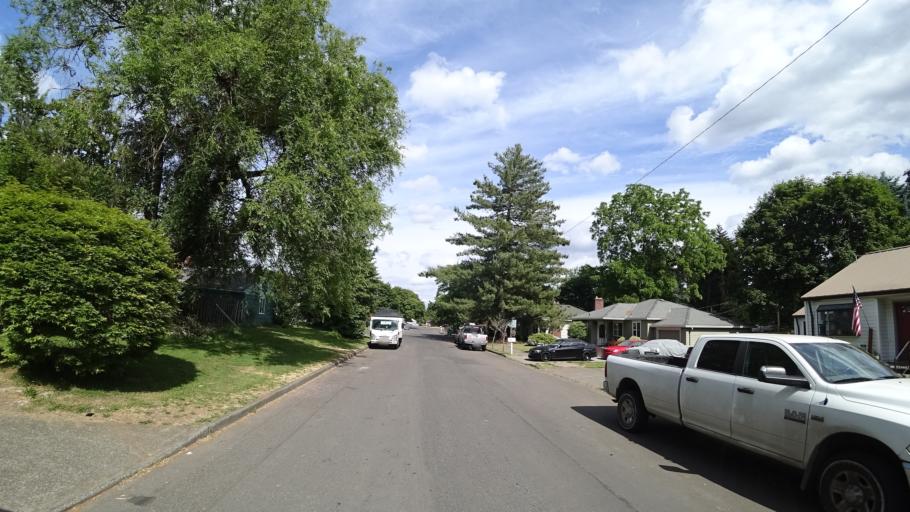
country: US
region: Oregon
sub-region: Multnomah County
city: Lents
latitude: 45.4957
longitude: -122.5459
